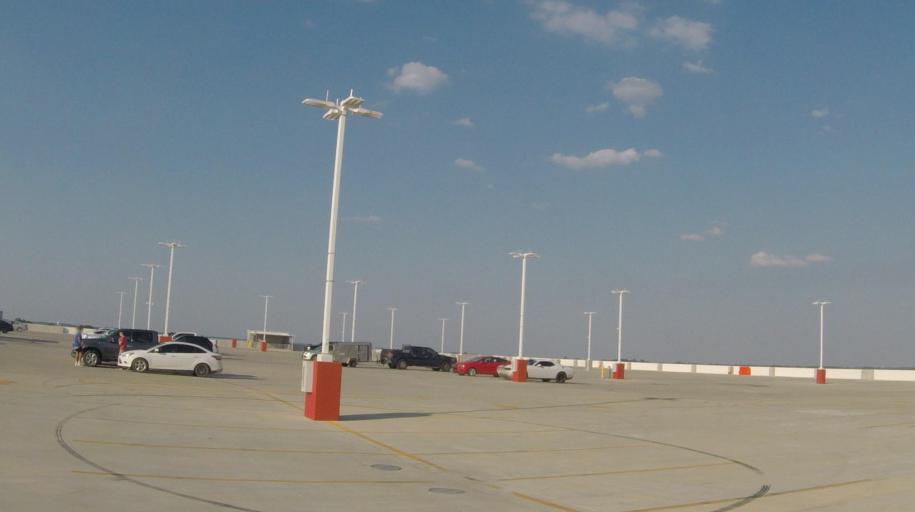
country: US
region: Oklahoma
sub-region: Bryan County
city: Calera
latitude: 33.9489
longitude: -96.4131
